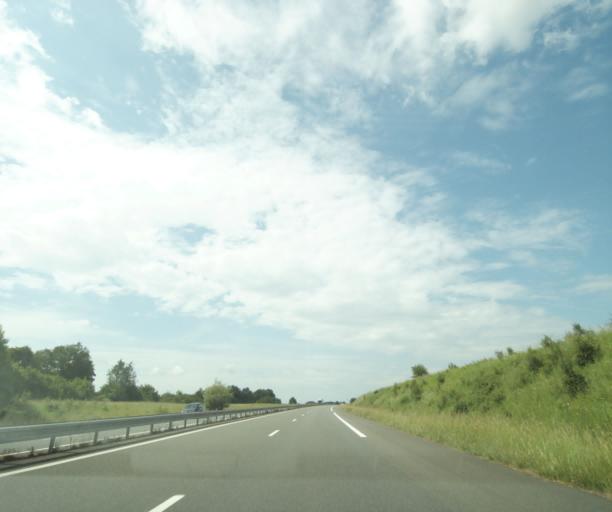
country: FR
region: Pays de la Loire
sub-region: Departement de Maine-et-Loire
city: Vivy
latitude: 47.3589
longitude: -0.0809
